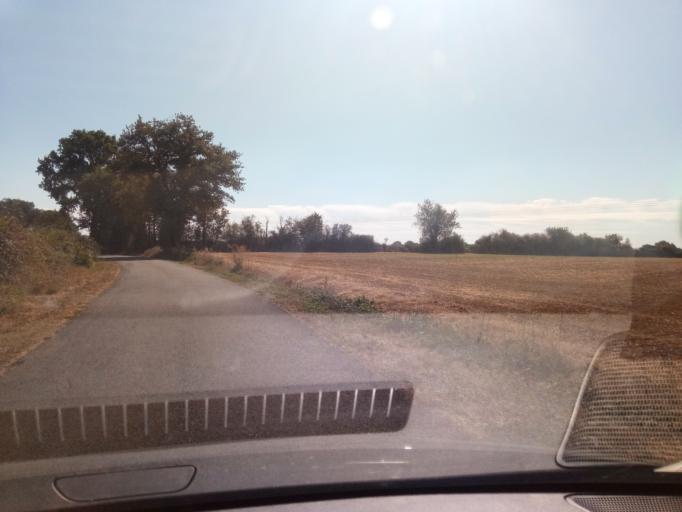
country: FR
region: Poitou-Charentes
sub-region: Departement de la Vienne
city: Lussac-les-Chateaux
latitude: 46.3992
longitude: 0.7439
